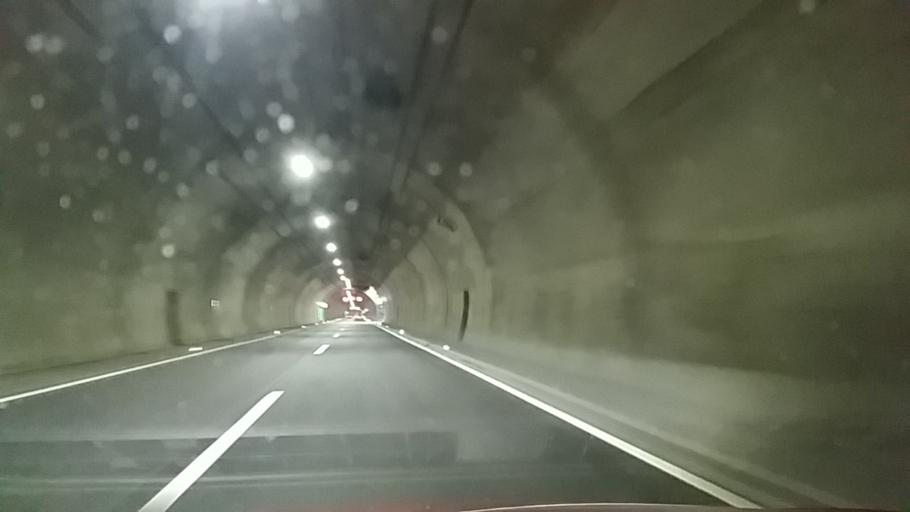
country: DE
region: Thuringia
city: Zella-Mehlis
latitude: 50.6290
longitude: 10.6655
